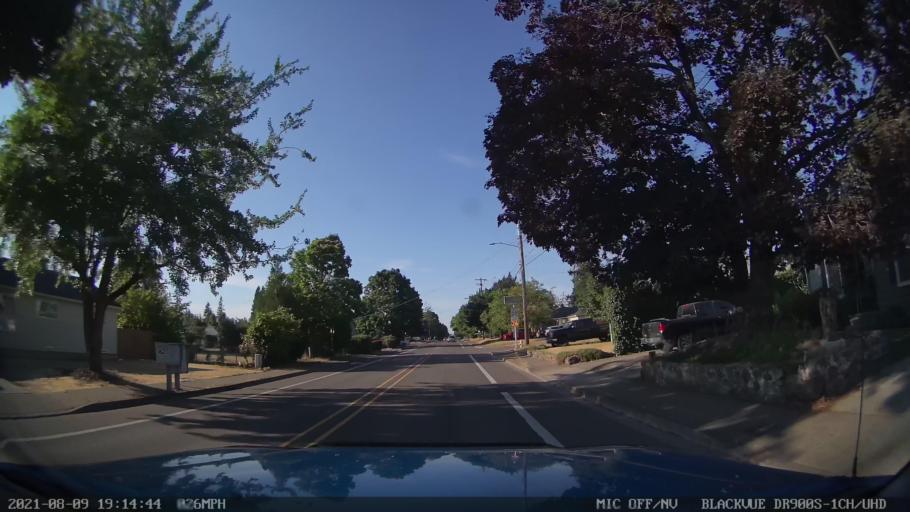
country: US
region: Oregon
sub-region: Marion County
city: Four Corners
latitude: 44.9350
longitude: -122.9917
